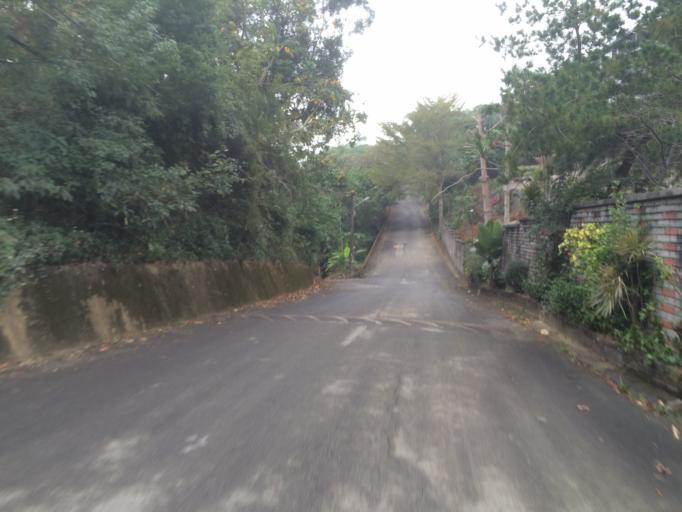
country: TW
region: Taiwan
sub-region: Taichung City
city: Taichung
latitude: 24.1602
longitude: 120.7610
